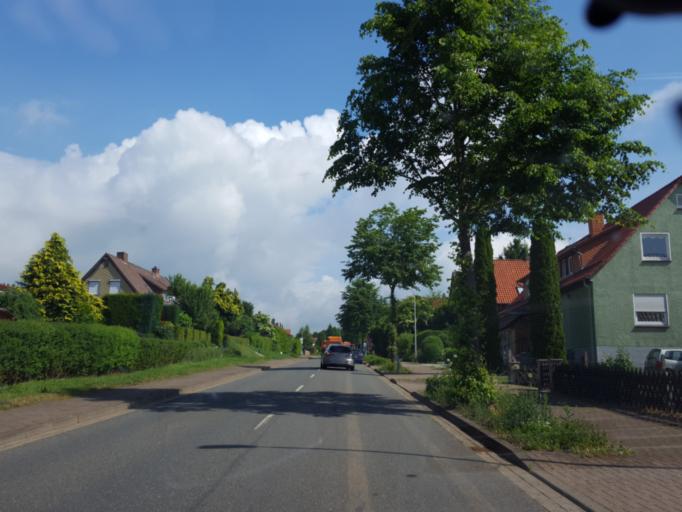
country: DE
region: Lower Saxony
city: Osterode am Harz
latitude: 51.7126
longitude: 10.2579
